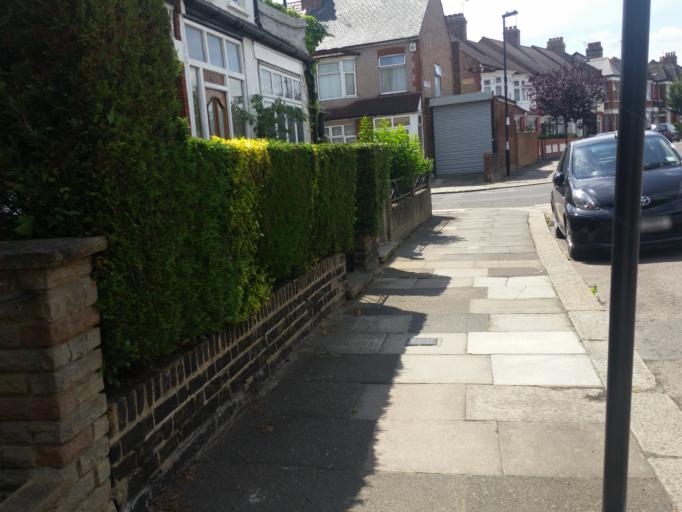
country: GB
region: England
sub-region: Greater London
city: Harringay
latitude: 51.5947
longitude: -0.0925
